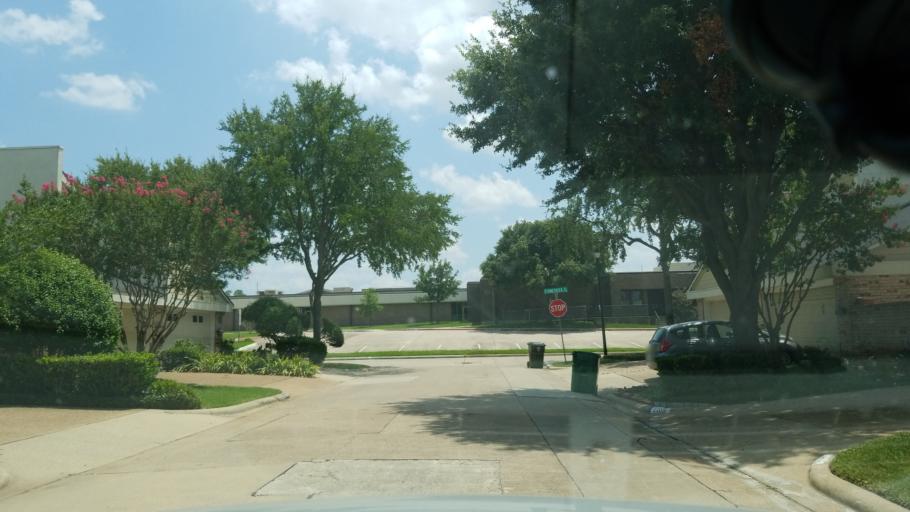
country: US
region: Texas
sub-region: Dallas County
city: Carrollton
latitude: 32.9683
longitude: -96.8636
